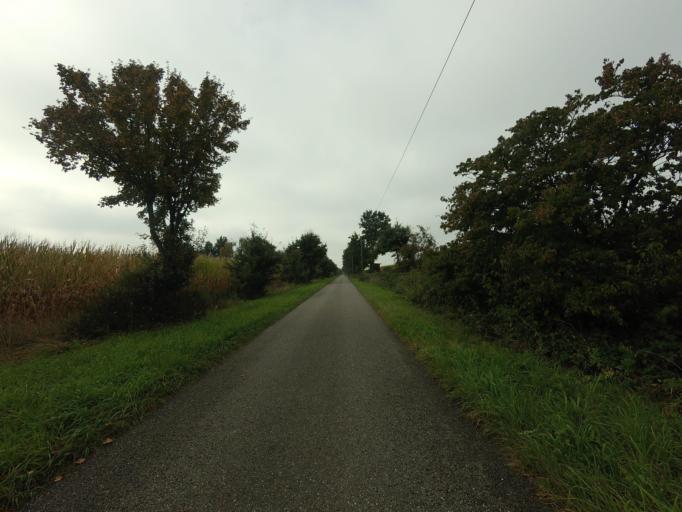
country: DE
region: Lower Saxony
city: Wielen
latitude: 52.5185
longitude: 6.7300
